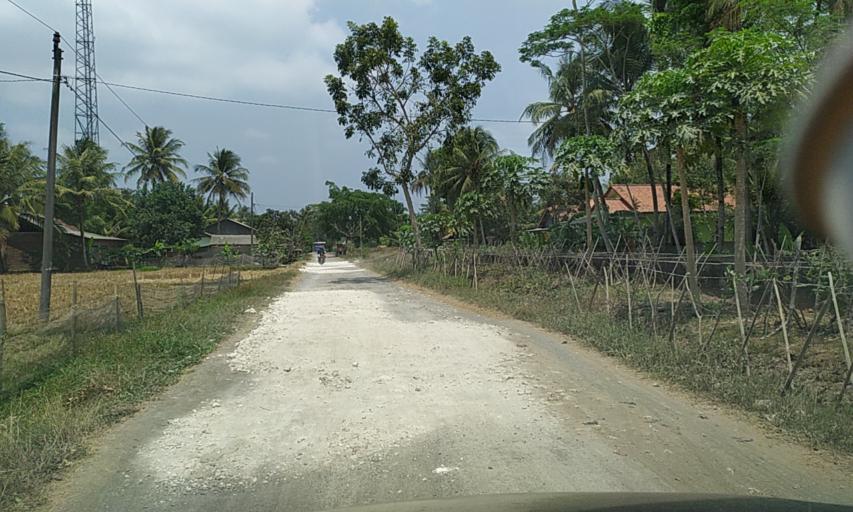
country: ID
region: Central Java
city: Sidakaya
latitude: -7.5779
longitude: 108.8626
